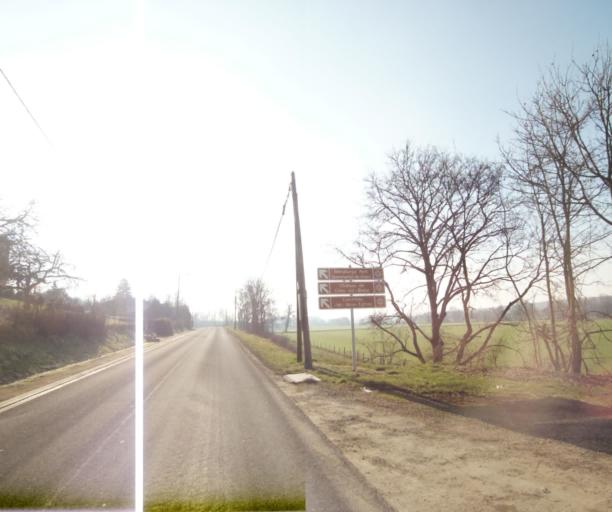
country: FR
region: Champagne-Ardenne
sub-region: Departement de la Haute-Marne
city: Wassy
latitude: 48.4677
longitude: 4.9699
